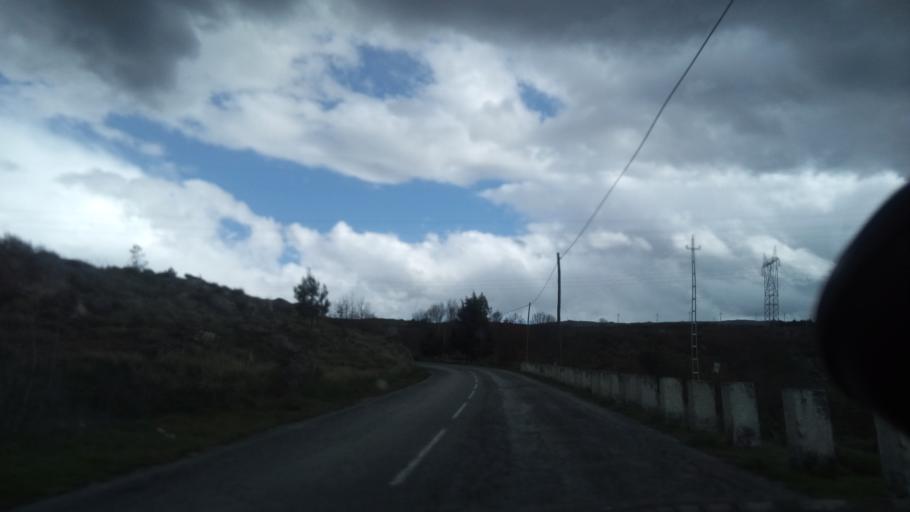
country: PT
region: Guarda
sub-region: Celorico da Beira
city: Celorico da Beira
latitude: 40.6260
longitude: -7.4324
